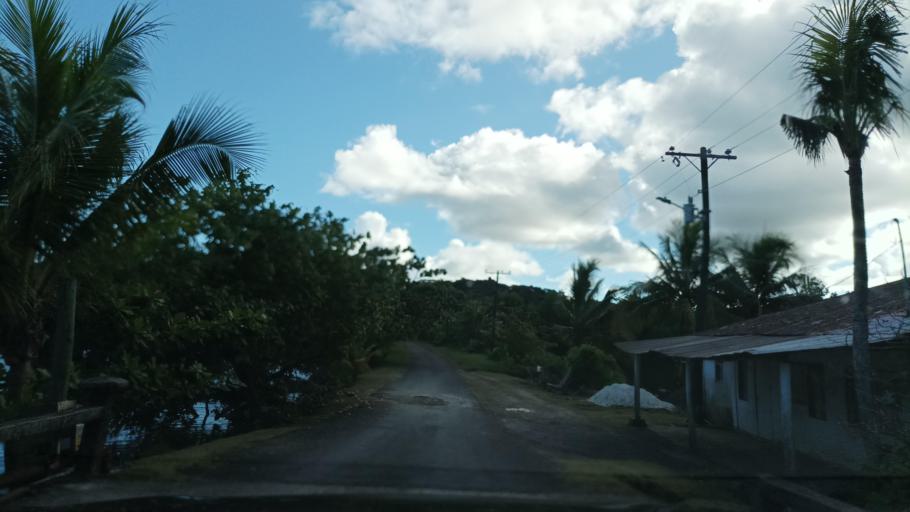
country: FM
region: Pohnpei
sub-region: Madolenihm Municipality
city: Madolenihm Municipality Government
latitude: 6.8450
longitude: 158.3140
